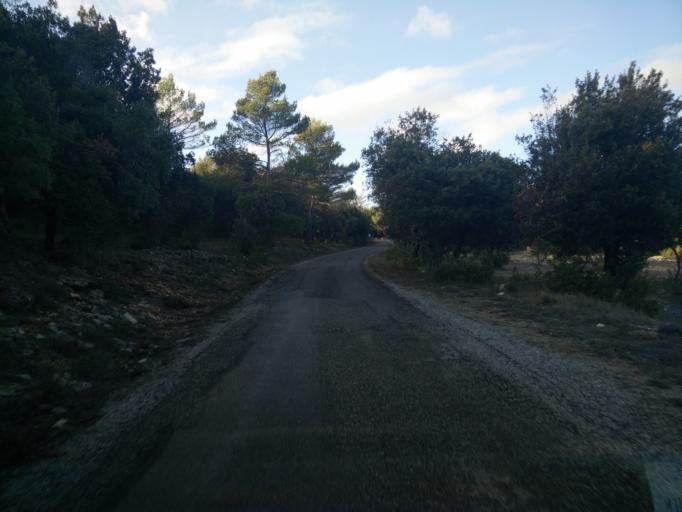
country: FR
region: Provence-Alpes-Cote d'Azur
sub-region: Departement du Var
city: Le Revest-les-Eaux
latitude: 43.2315
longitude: 5.9105
